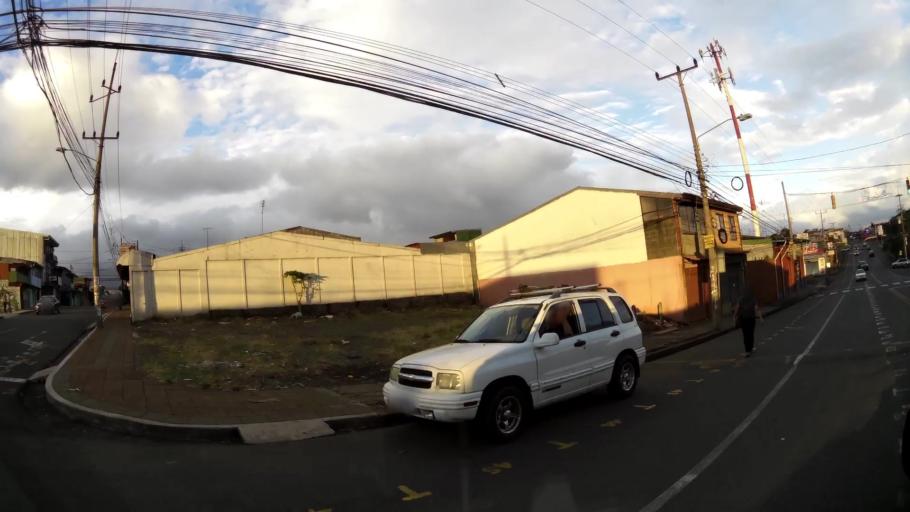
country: CR
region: Heredia
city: San Francisco
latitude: 9.9934
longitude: -84.1217
